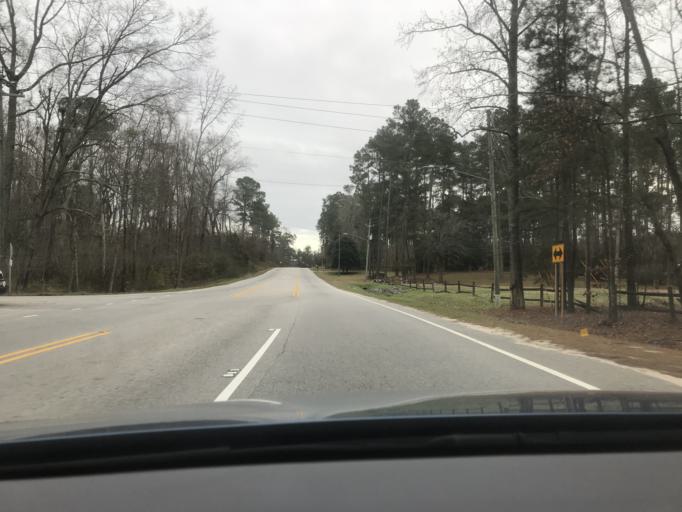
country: US
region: North Carolina
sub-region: Hoke County
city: Rockfish
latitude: 35.0504
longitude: -79.0113
